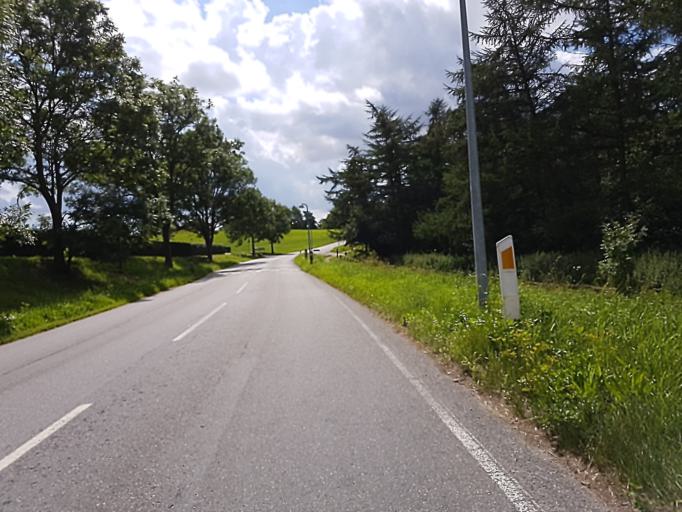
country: DK
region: Capital Region
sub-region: Ballerup Kommune
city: Malov
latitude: 55.7910
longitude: 12.3234
